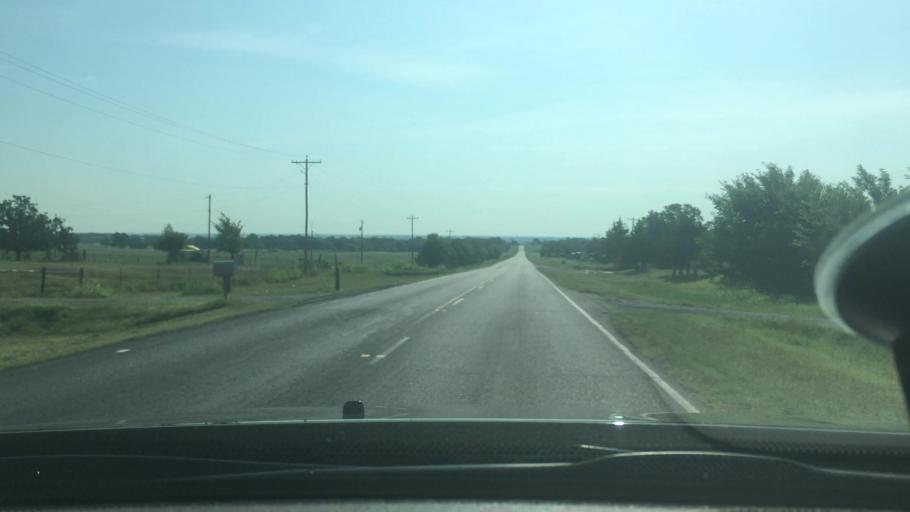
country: US
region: Oklahoma
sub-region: Garvin County
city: Wynnewood
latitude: 34.6518
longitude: -97.2429
